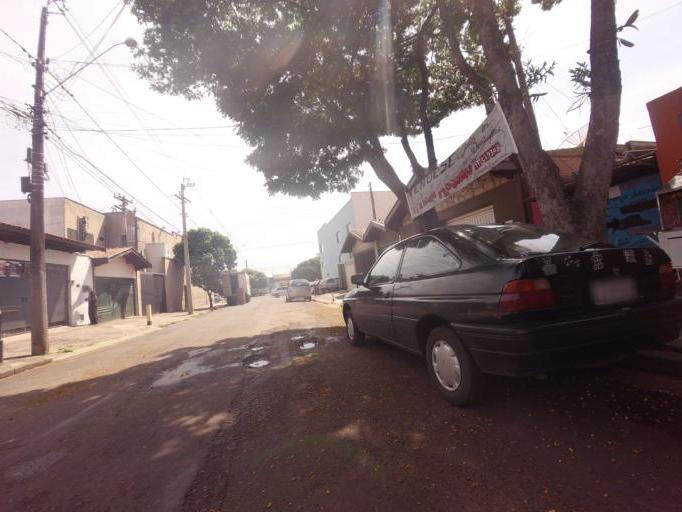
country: BR
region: Sao Paulo
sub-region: Piracicaba
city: Piracicaba
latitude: -22.7674
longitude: -47.5889
